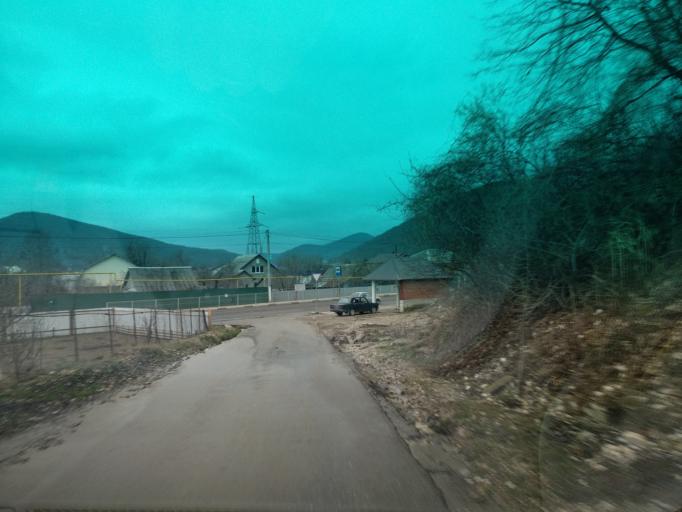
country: RU
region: Krasnodarskiy
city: Novomikhaylovskiy
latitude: 44.2581
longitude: 38.8622
